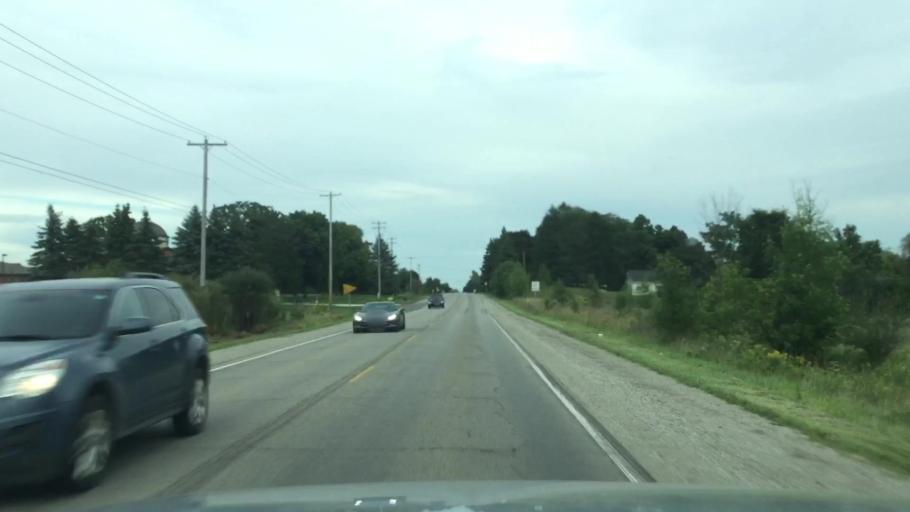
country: US
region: Michigan
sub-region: Genesee County
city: Grand Blanc
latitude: 42.8862
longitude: -83.6629
